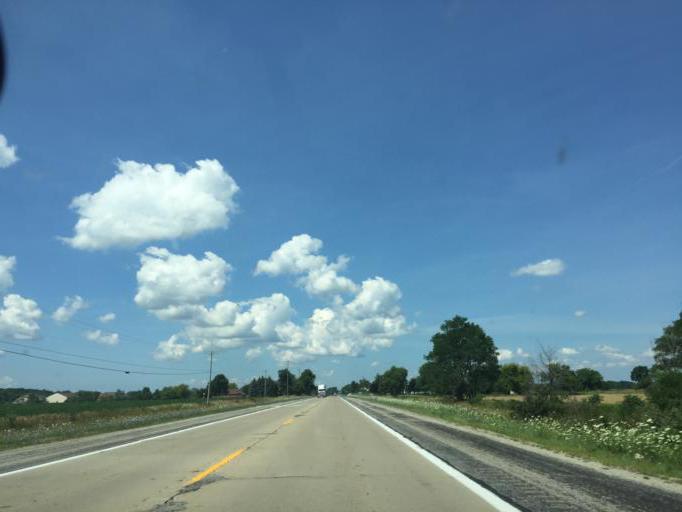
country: US
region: Ohio
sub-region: Lucas County
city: Sylvania
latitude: 41.7972
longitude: -83.7089
